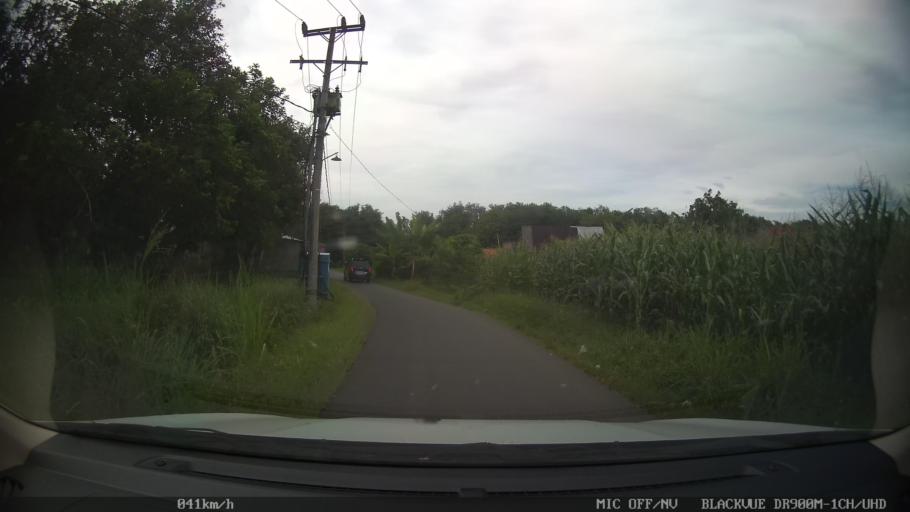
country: ID
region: North Sumatra
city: Sunggal
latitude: 3.6547
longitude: 98.5901
